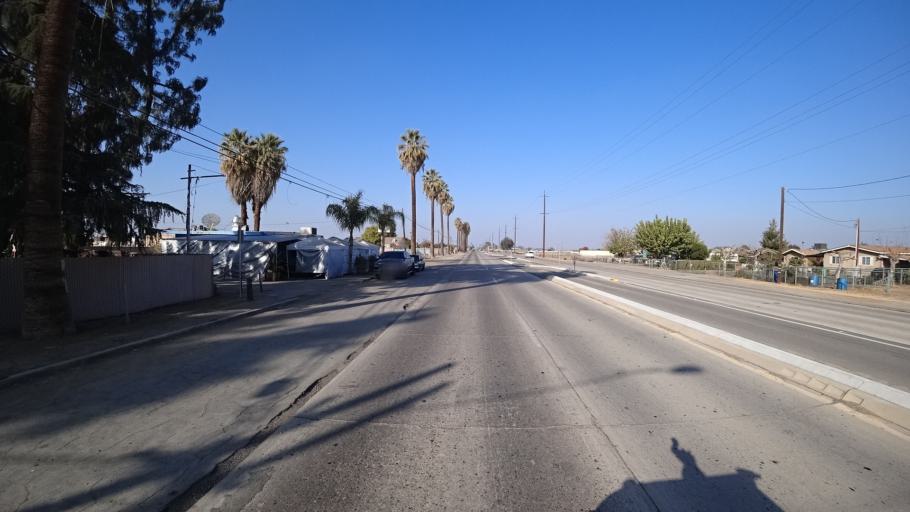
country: US
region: California
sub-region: Kern County
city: Greenfield
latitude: 35.2772
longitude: -119.0032
